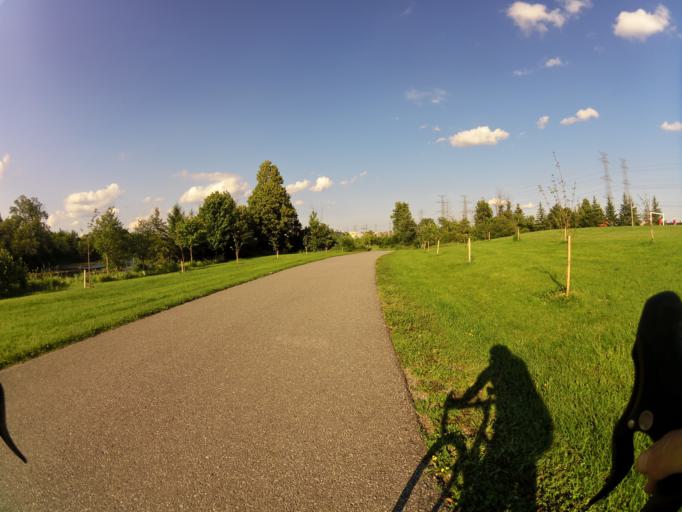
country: CA
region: Ontario
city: Ottawa
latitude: 45.3466
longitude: -75.7137
